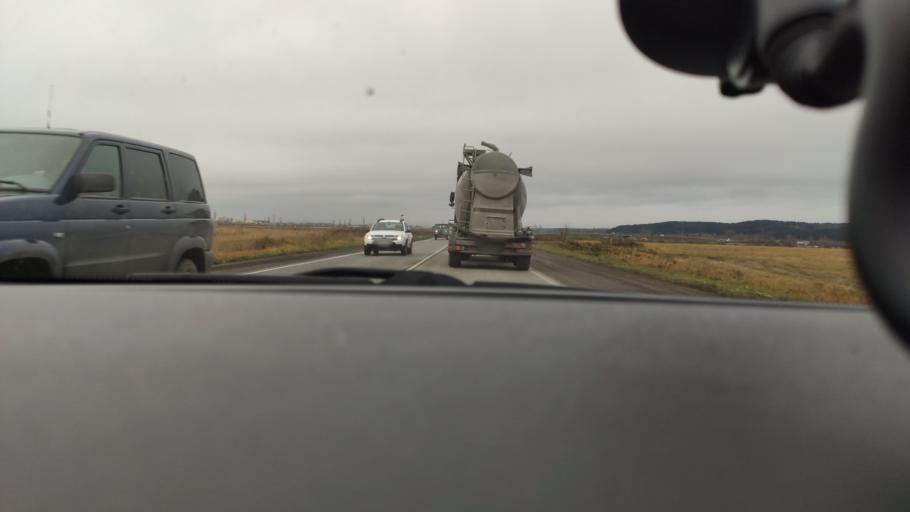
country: RU
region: Perm
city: Froly
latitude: 57.9201
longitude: 56.1803
